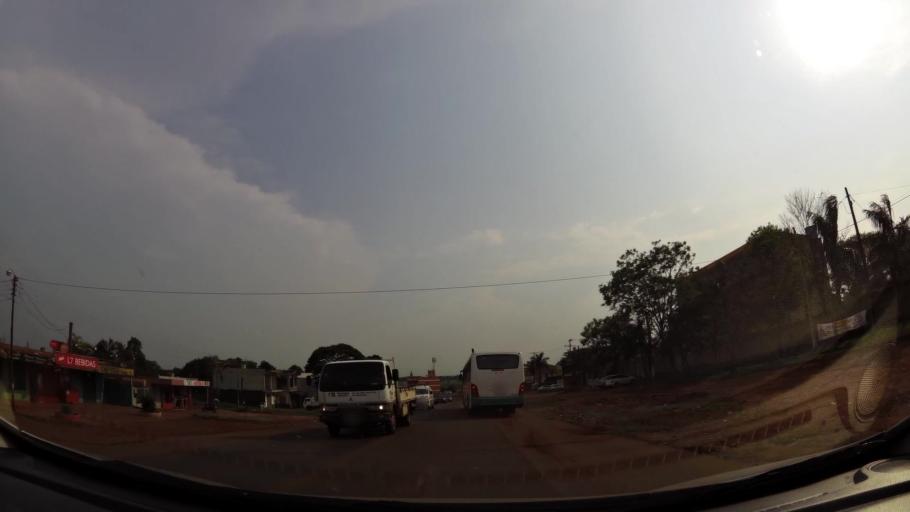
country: PY
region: Alto Parana
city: Ciudad del Este
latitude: -25.4877
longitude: -54.6627
